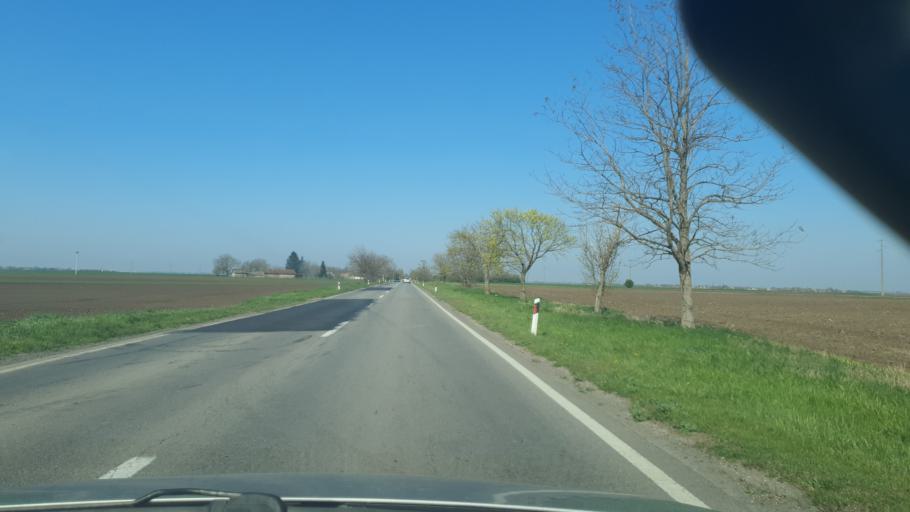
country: RS
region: Autonomna Pokrajina Vojvodina
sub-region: Zapadnobacki Okrug
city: Sombor
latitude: 45.7680
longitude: 19.2208
